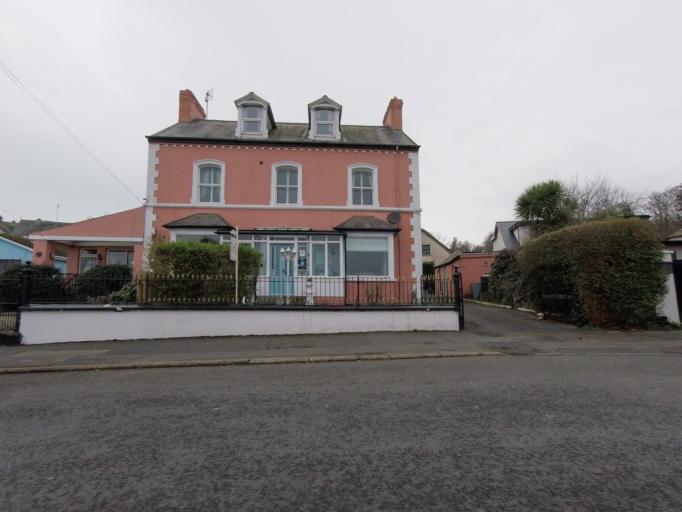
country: IE
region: Munster
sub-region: Waterford
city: Dunmore East
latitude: 52.1491
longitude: -6.9946
